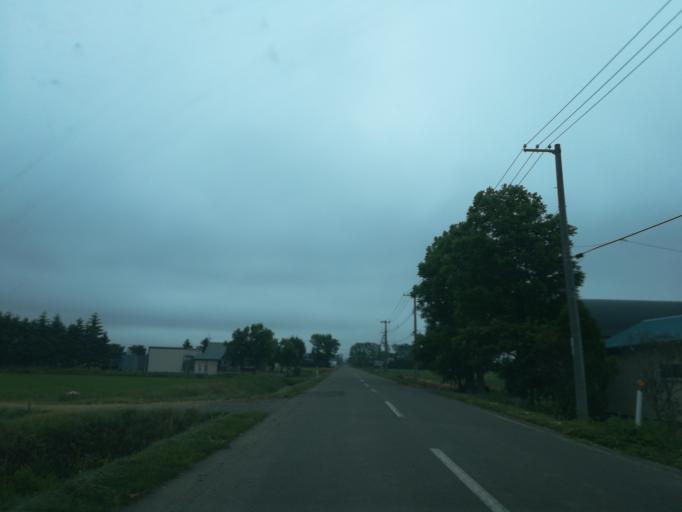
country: JP
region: Hokkaido
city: Ebetsu
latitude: 43.0652
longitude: 141.6325
